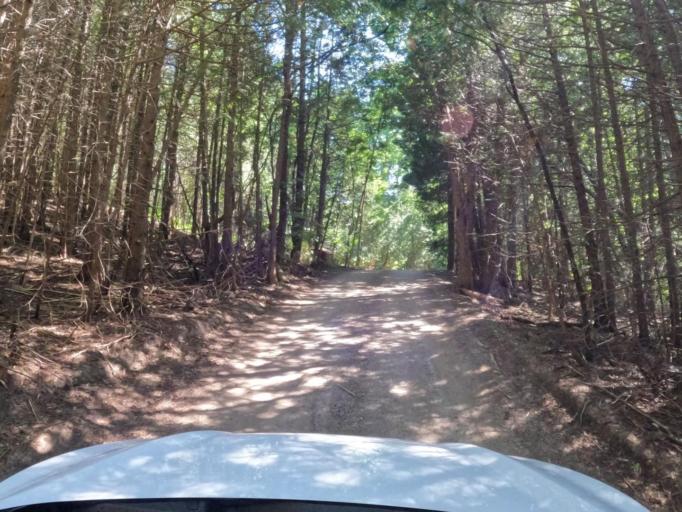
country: CA
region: Ontario
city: Cambridge
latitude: 43.4187
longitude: -80.2517
